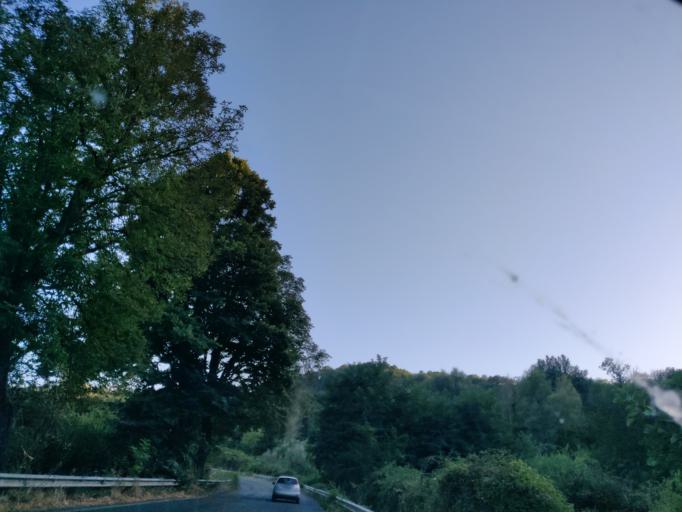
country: IT
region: Latium
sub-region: Provincia di Viterbo
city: Acquapendente
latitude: 42.7528
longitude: 11.8651
